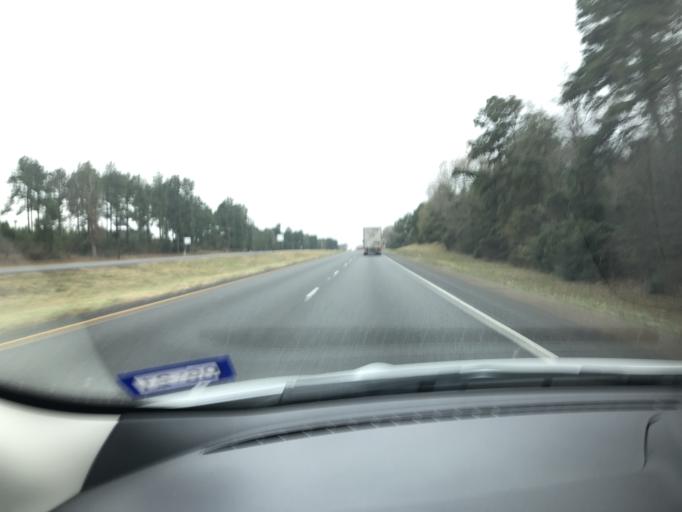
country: US
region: Texas
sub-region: Nacogdoches County
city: Nacogdoches
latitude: 31.5142
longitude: -94.6995
